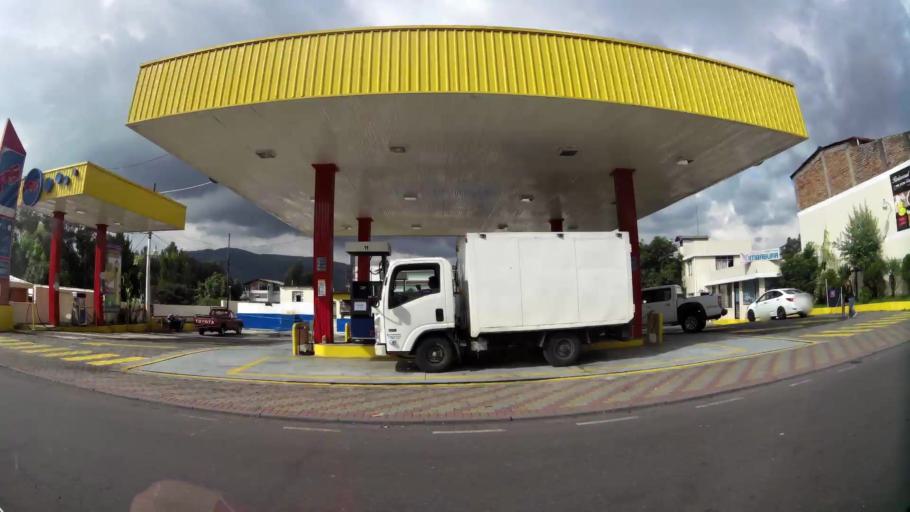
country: EC
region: Pichincha
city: Sangolqui
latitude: -0.3089
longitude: -78.4524
